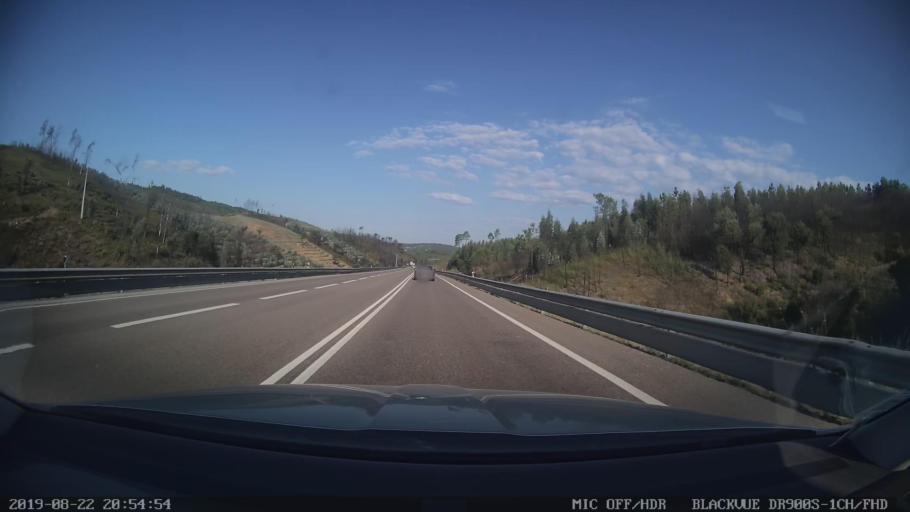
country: PT
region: Castelo Branco
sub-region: Serta
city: Serta
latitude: 39.7773
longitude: -8.0216
